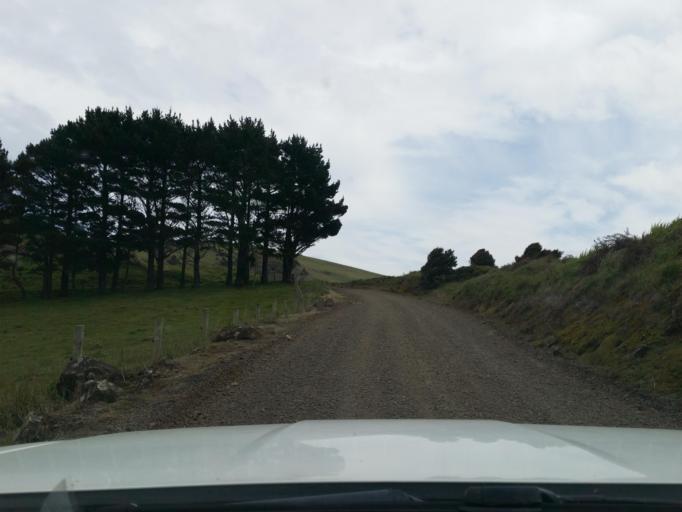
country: NZ
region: Northland
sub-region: Kaipara District
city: Dargaville
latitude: -35.7335
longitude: 173.5859
